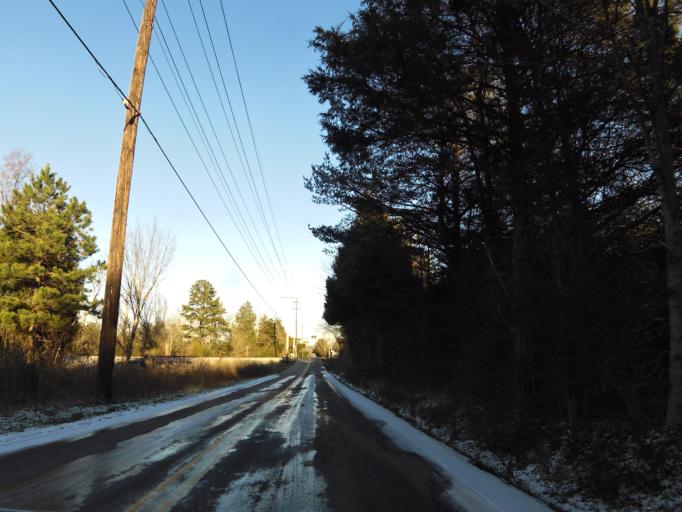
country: US
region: Tennessee
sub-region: Knox County
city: Farragut
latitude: 35.9703
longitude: -84.0731
